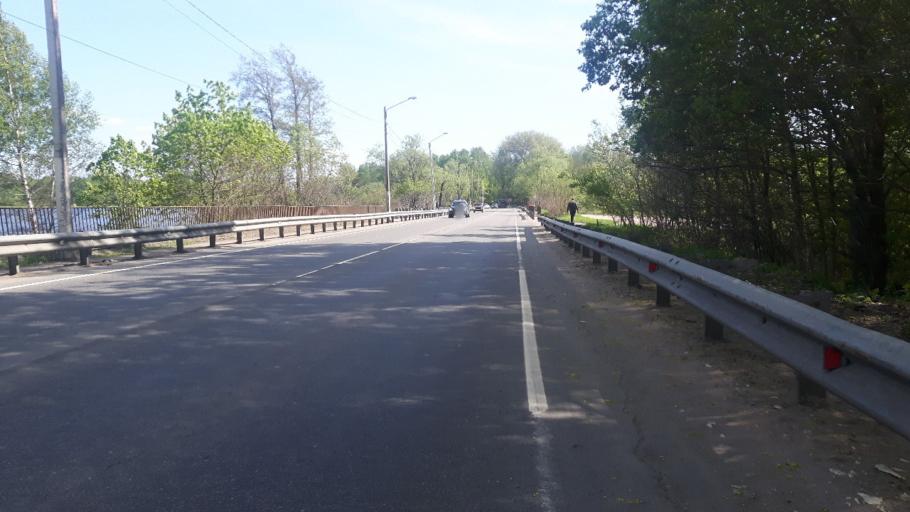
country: RU
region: Leningrad
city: Vyborg
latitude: 60.7266
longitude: 28.7063
